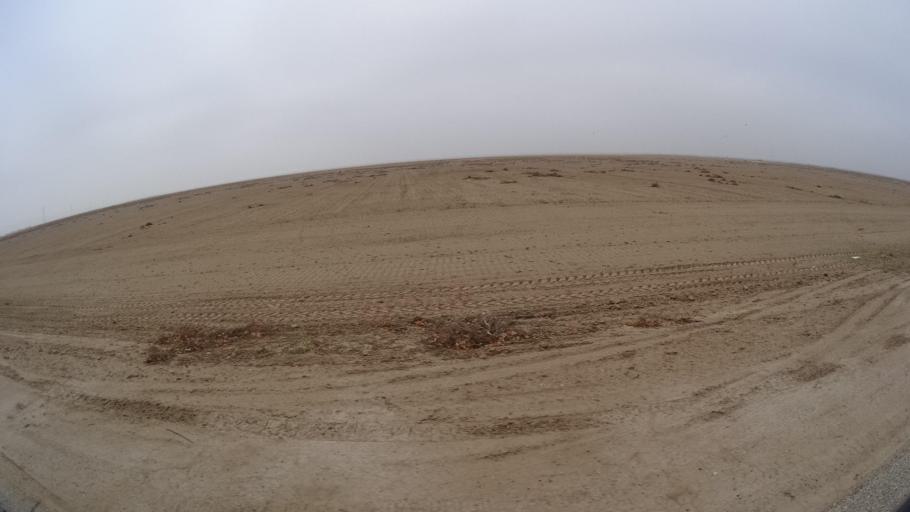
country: US
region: California
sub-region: Kern County
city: Maricopa
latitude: 35.1228
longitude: -119.2915
